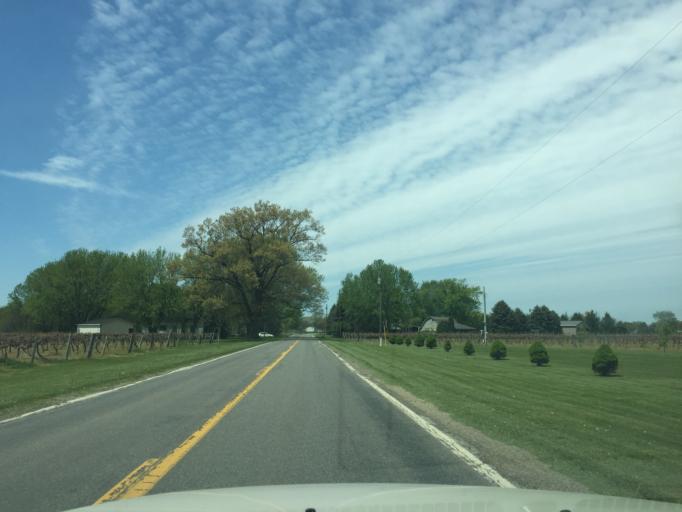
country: US
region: Michigan
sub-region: Berrien County
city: Stevensville
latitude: 41.9489
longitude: -86.4775
